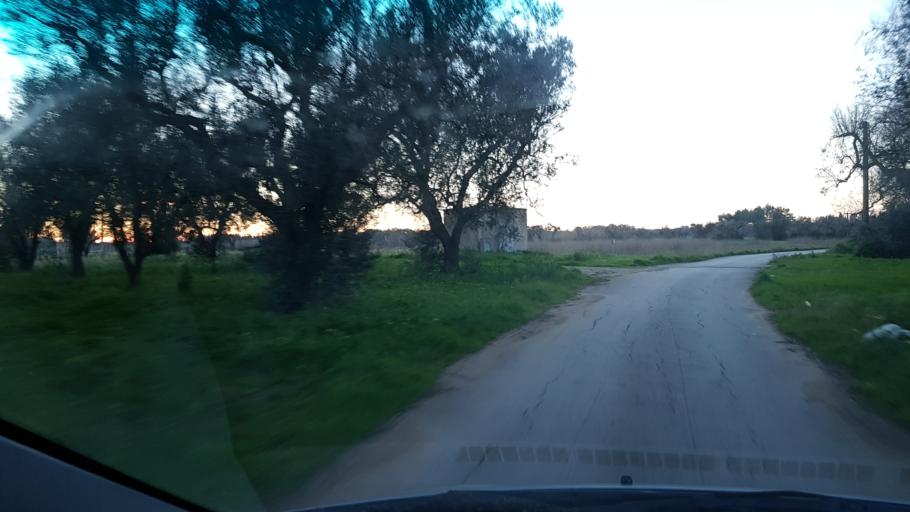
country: IT
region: Apulia
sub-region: Provincia di Brindisi
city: San Pietro Vernotico
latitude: 40.5001
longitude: 17.9823
